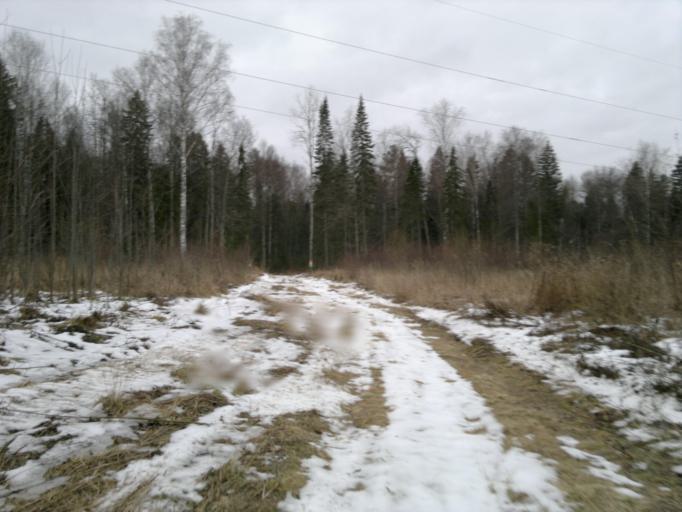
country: RU
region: Mariy-El
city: Yoshkar-Ola
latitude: 56.5955
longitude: 47.9692
